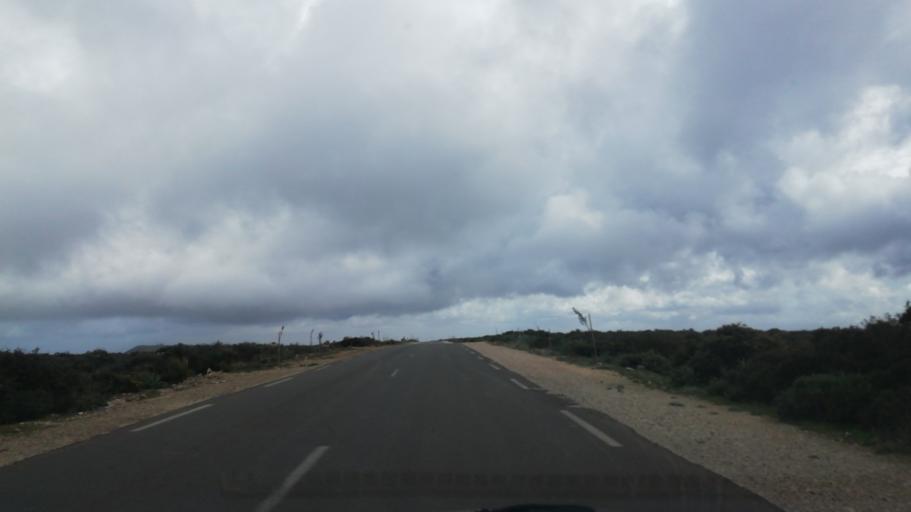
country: DZ
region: Oran
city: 'Ain el Turk
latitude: 35.6995
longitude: -0.7624
